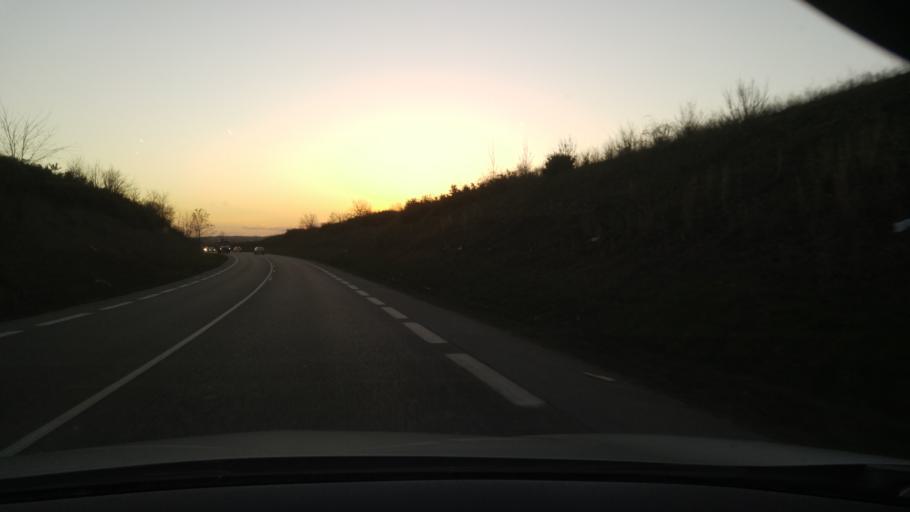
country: FR
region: Rhone-Alpes
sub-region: Departement de l'Isere
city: Satolas-et-Bonce
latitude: 45.7030
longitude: 5.0998
